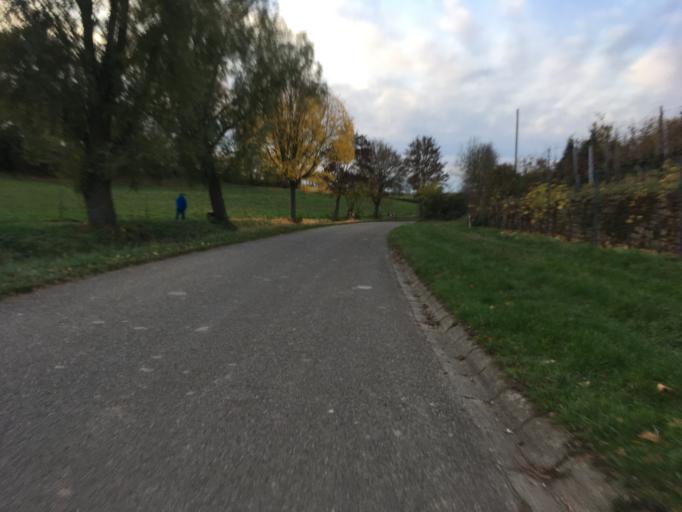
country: DE
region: Baden-Wuerttemberg
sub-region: Regierungsbezirk Stuttgart
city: Neckarwestheim
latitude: 49.0384
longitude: 9.1907
